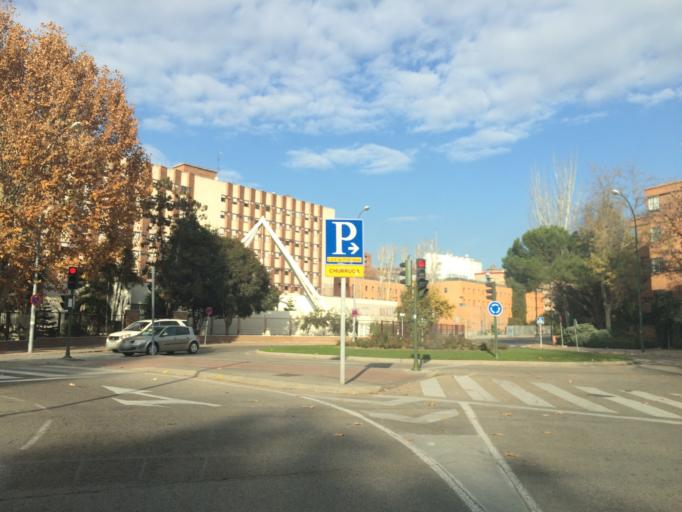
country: ES
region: Madrid
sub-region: Provincia de Madrid
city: Tetuan de las Victorias
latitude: 40.4489
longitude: -3.7165
